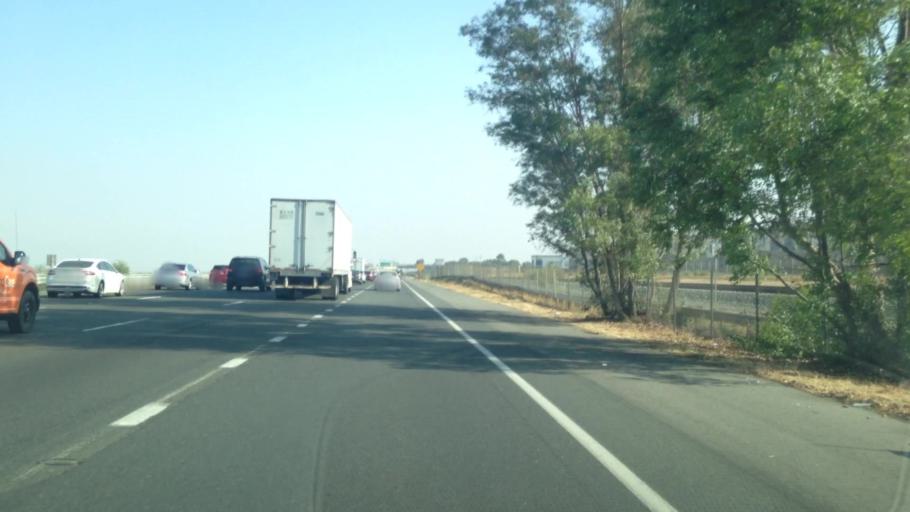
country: US
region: California
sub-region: Riverside County
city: March Air Force Base
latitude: 33.8975
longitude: -117.2751
